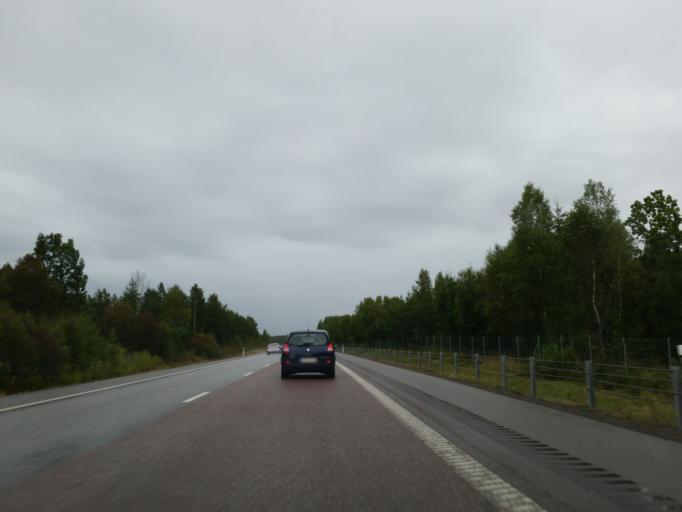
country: SE
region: Uppsala
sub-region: Enkopings Kommun
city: Dalby
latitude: 59.6099
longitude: 17.4167
